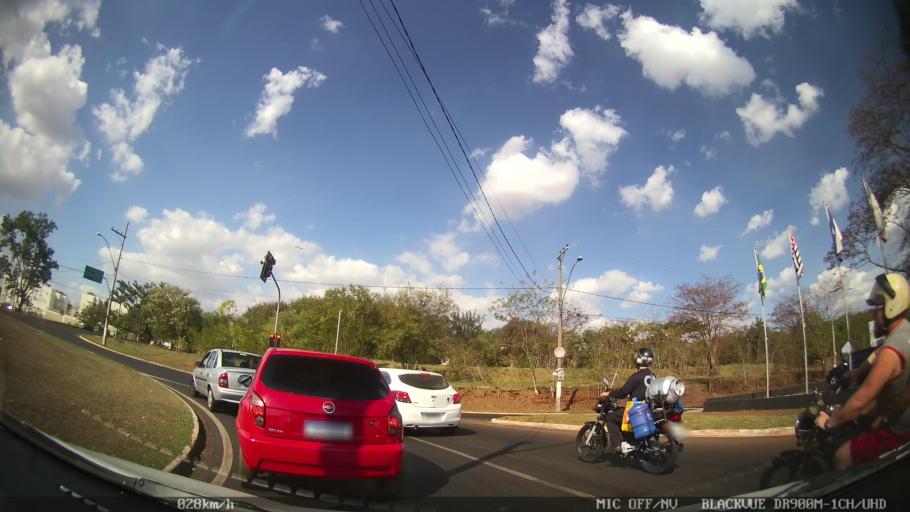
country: BR
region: Sao Paulo
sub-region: Ribeirao Preto
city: Ribeirao Preto
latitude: -21.2041
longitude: -47.8273
